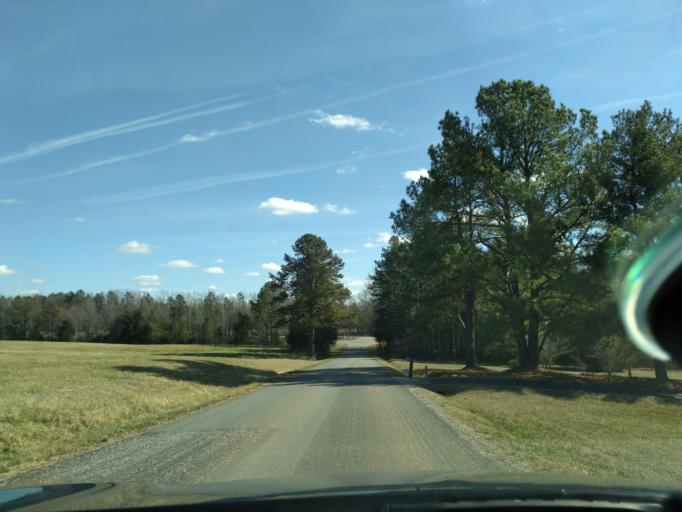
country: US
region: Virginia
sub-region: Nottoway County
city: Crewe
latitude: 37.1697
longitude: -78.2534
